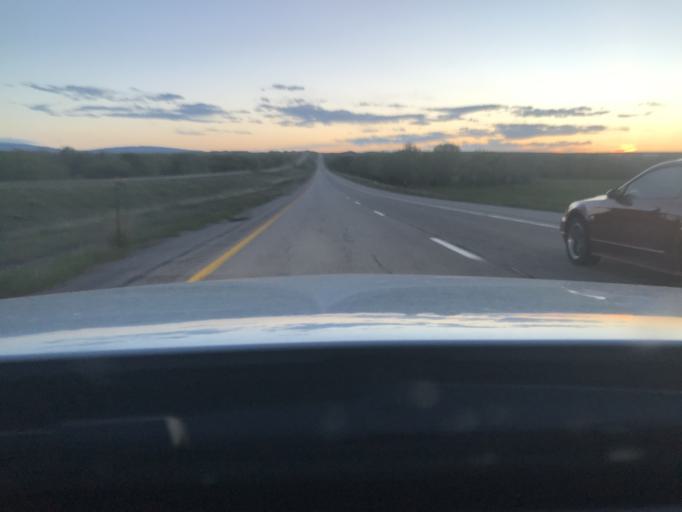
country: US
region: Wyoming
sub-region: Converse County
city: Glenrock
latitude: 42.8374
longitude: -105.8631
